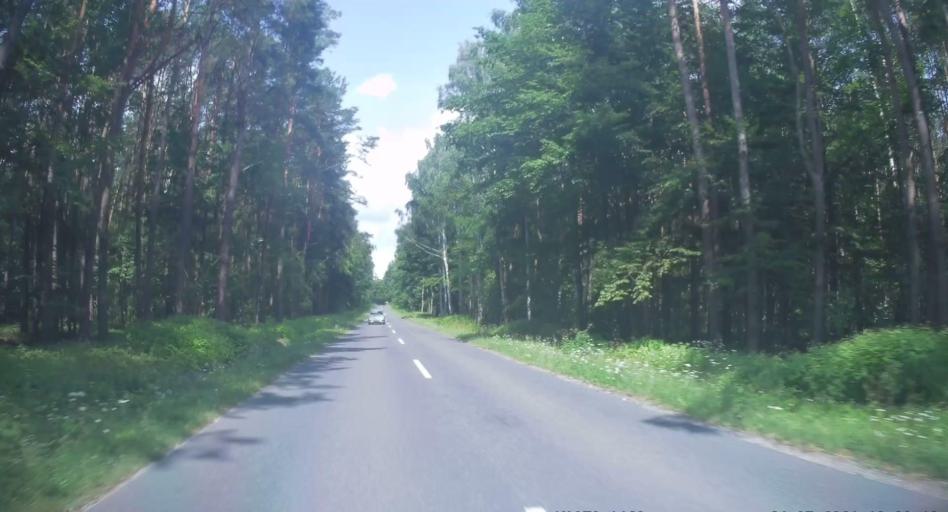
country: PL
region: Lodz Voivodeship
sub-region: Powiat tomaszowski
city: Lubochnia
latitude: 51.5592
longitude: 20.1295
